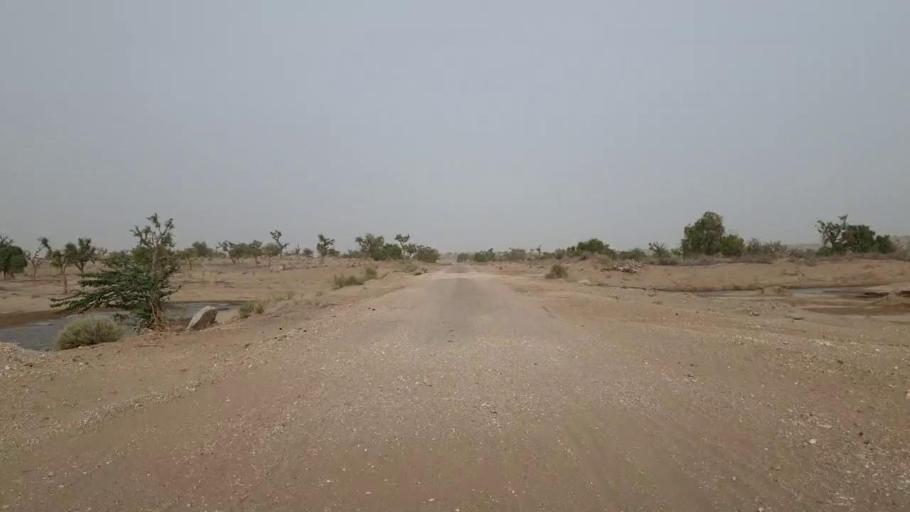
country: PK
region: Sindh
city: Islamkot
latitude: 24.5451
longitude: 70.3739
